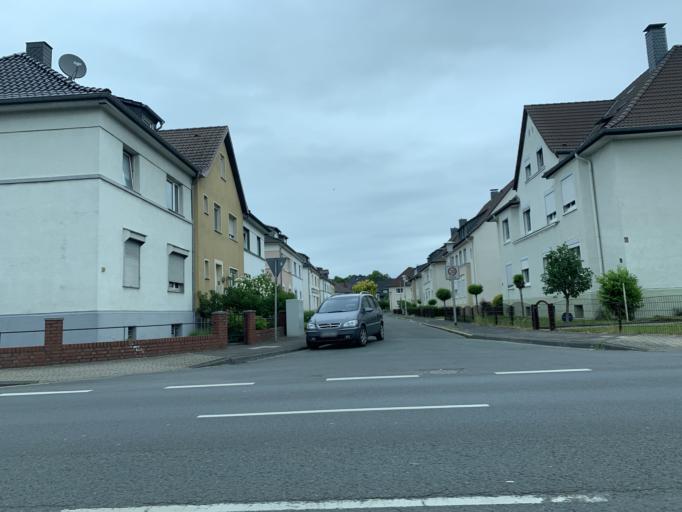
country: DE
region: North Rhine-Westphalia
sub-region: Regierungsbezirk Arnsberg
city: Hamm
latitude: 51.6671
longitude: 7.8283
